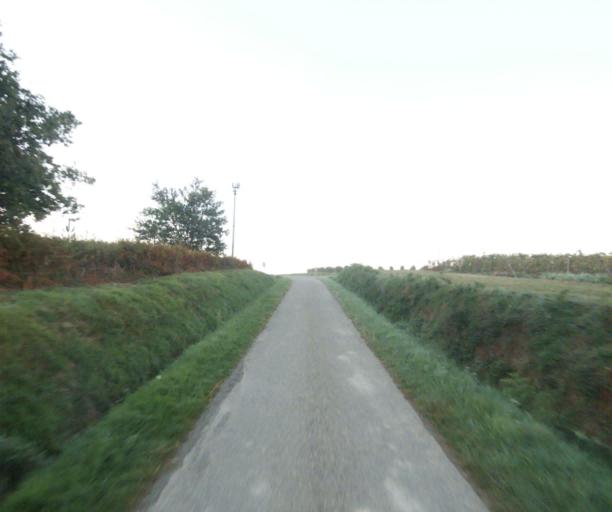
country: FR
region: Midi-Pyrenees
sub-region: Departement du Gers
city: Vic-Fezensac
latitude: 43.7851
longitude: 0.2374
